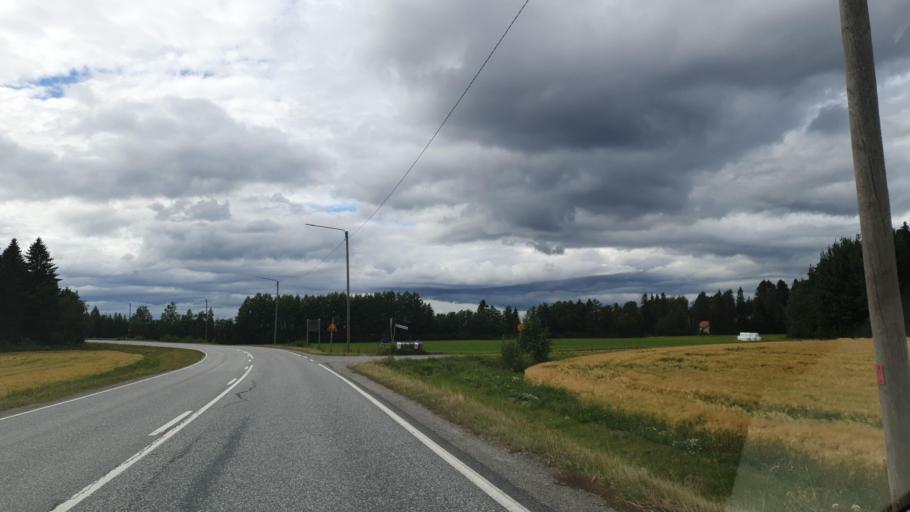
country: FI
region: Northern Savo
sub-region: Ylae-Savo
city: Iisalmi
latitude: 63.5205
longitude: 27.2196
